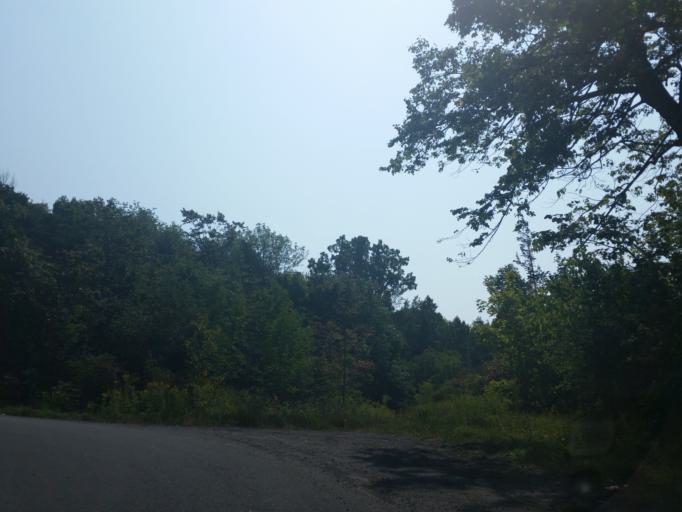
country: CA
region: Ontario
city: Picton
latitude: 44.0027
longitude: -77.1361
